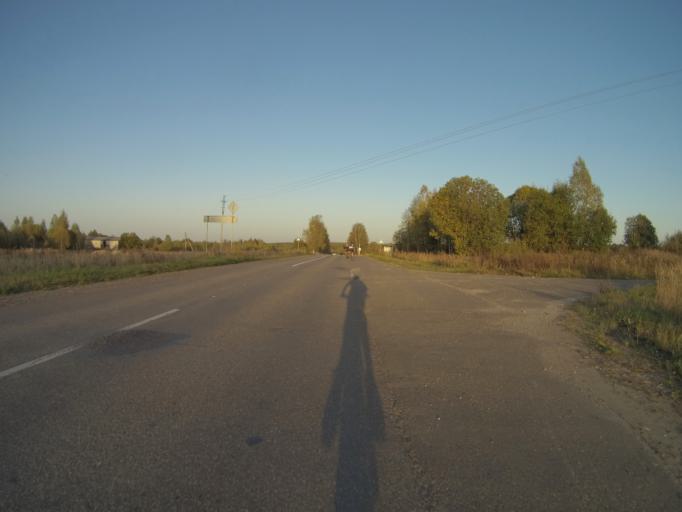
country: RU
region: Vladimir
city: Golovino
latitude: 55.9603
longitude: 40.4894
